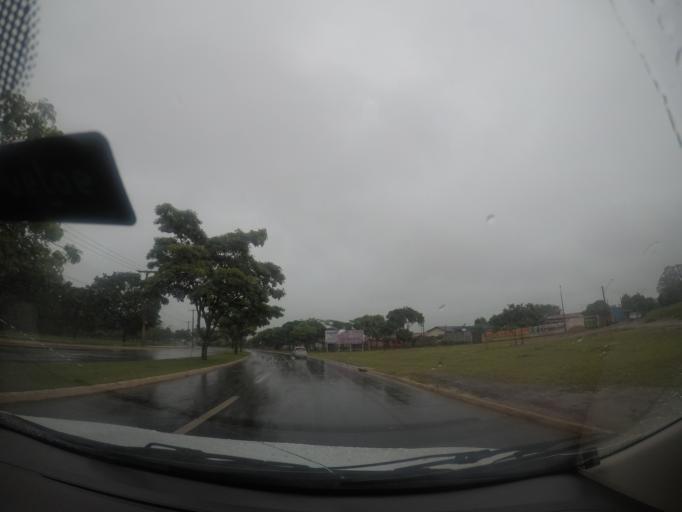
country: BR
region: Goias
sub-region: Goiania
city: Goiania
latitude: -16.6014
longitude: -49.3313
